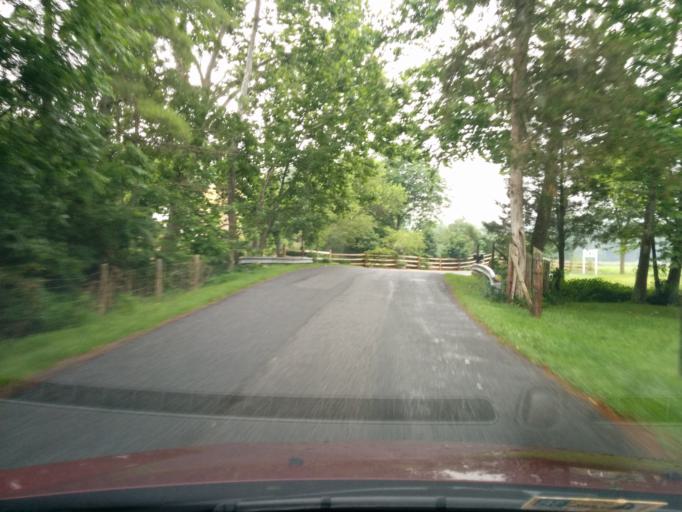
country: US
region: Virginia
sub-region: Rockbridge County
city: East Lexington
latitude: 37.8979
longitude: -79.4164
